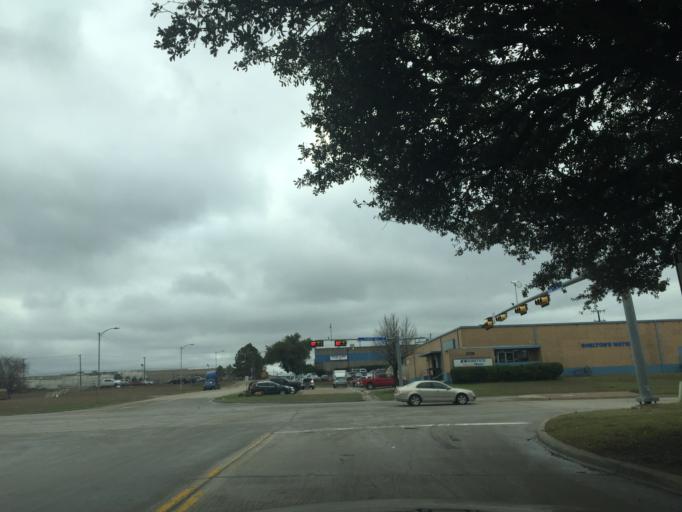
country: US
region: Texas
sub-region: Tarrant County
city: Arlington
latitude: 32.7492
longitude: -97.0600
